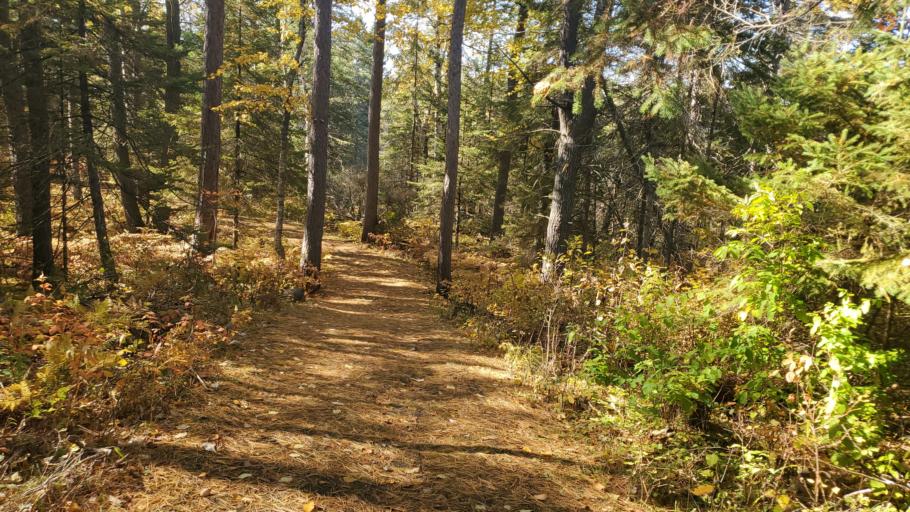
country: CA
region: Ontario
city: Peterborough
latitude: 44.6204
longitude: -78.0463
